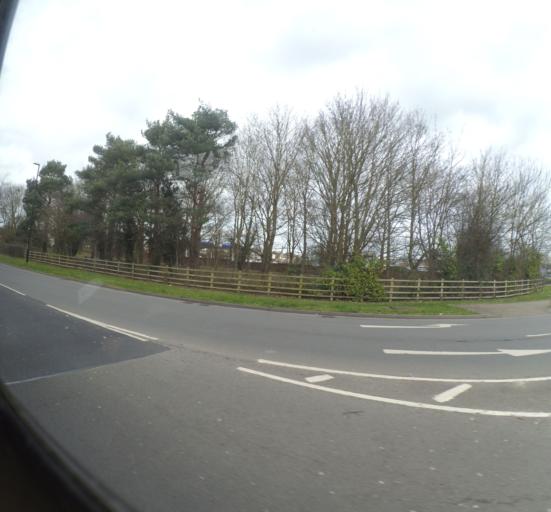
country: GB
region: England
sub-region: Warwickshire
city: Ryton on Dunsmore
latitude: 52.4132
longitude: -1.4441
